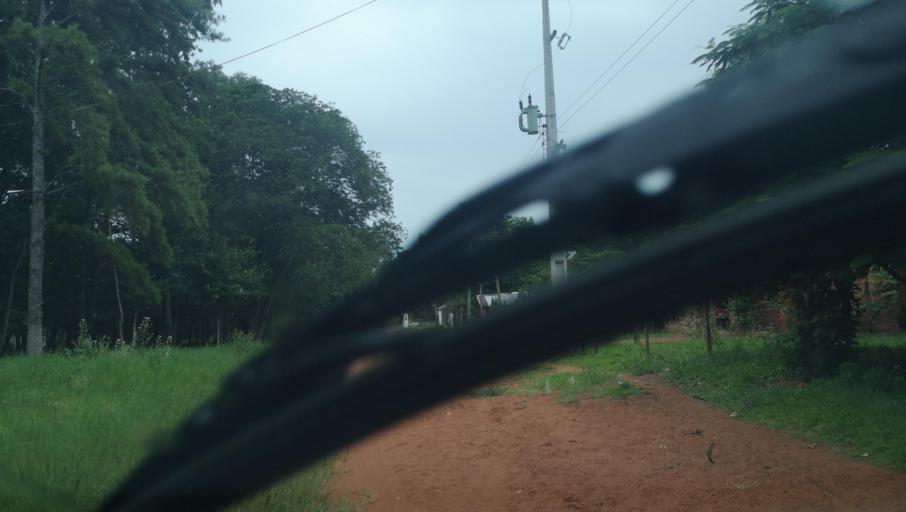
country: PY
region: San Pedro
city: Capiibary
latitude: -24.7280
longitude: -56.0116
